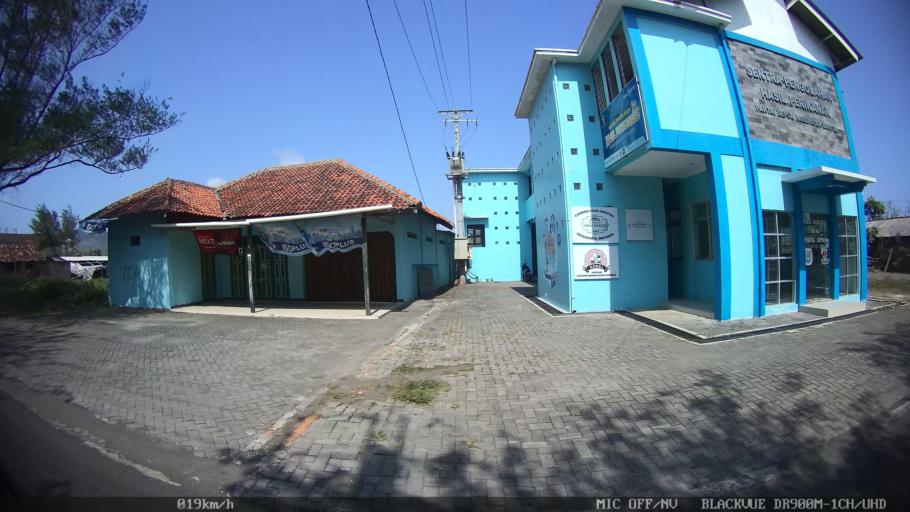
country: ID
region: Daerah Istimewa Yogyakarta
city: Bambanglipuro
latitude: -8.0121
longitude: 110.2940
